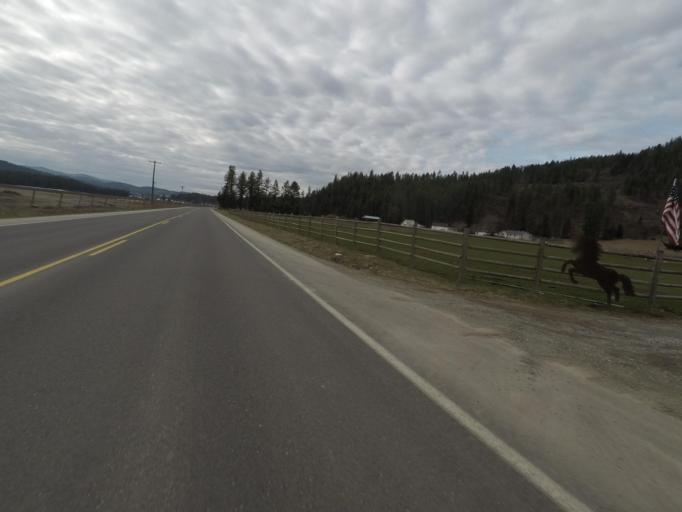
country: US
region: Washington
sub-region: Stevens County
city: Colville
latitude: 48.5709
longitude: -117.8793
